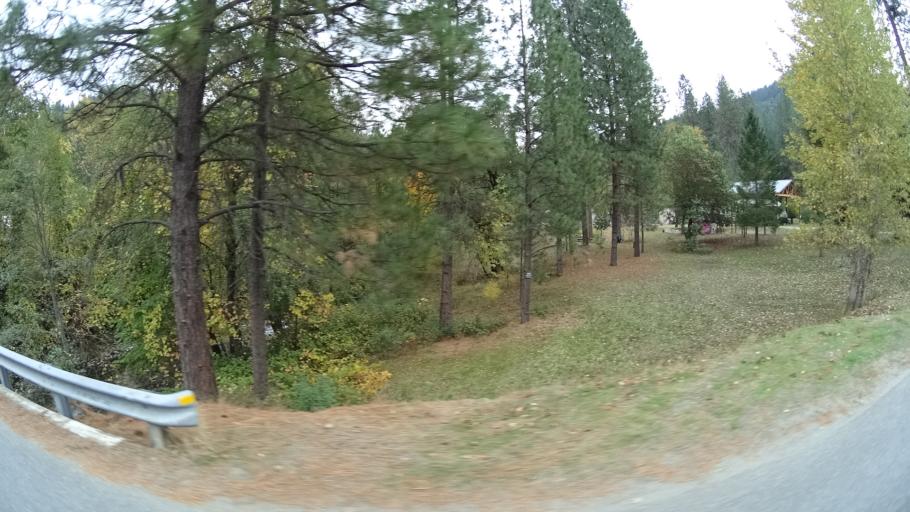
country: US
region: California
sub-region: Siskiyou County
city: Happy Camp
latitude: 41.7805
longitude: -123.3929
